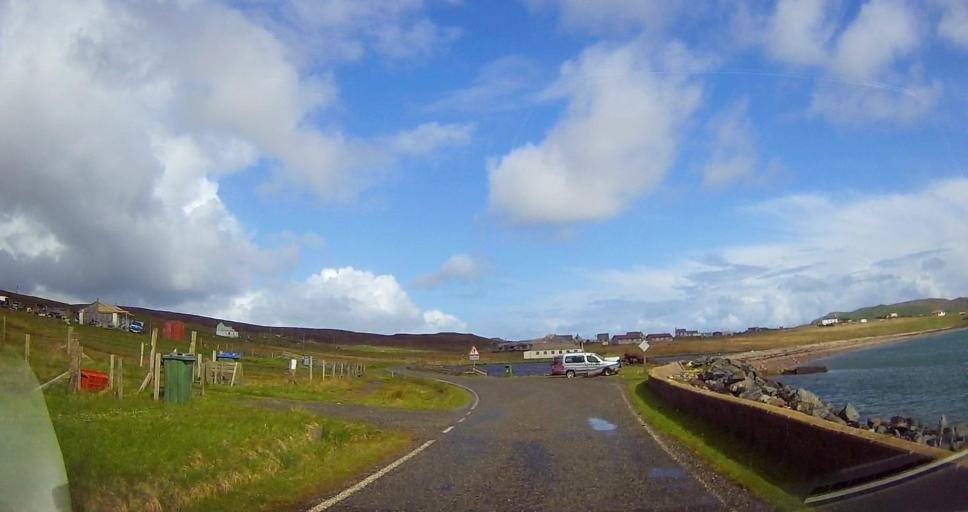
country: GB
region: Scotland
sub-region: Shetland Islands
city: Lerwick
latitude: 60.5826
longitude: -1.3356
